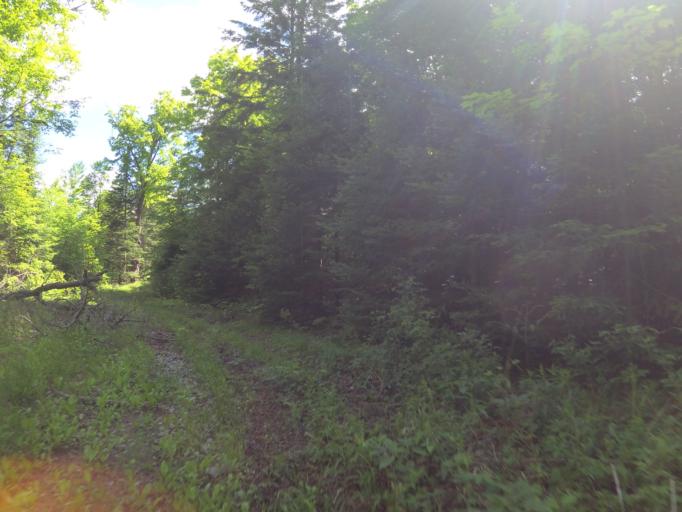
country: CA
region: Ontario
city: Renfrew
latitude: 45.0500
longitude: -76.7611
